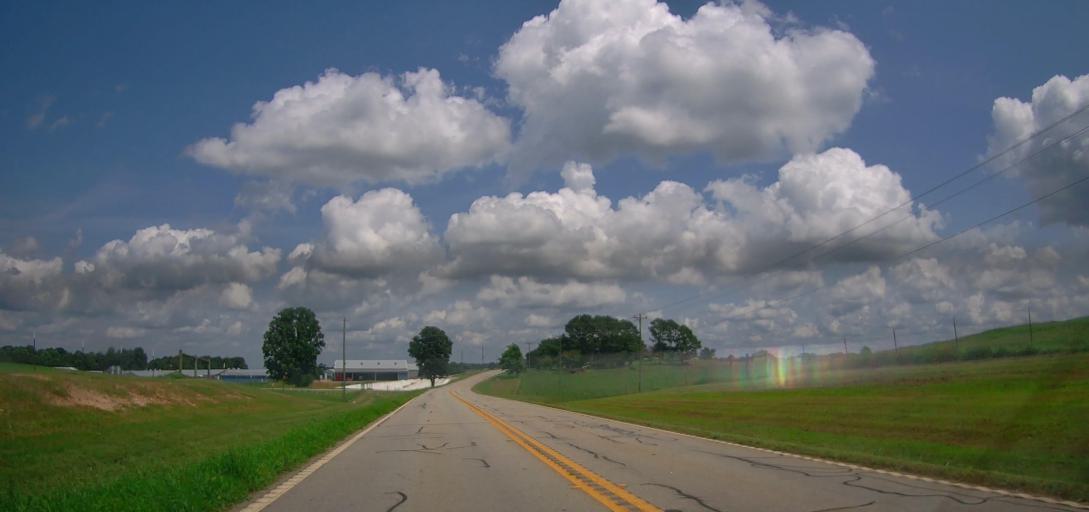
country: US
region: Georgia
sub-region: Heard County
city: Franklin
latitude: 33.3672
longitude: -85.2300
